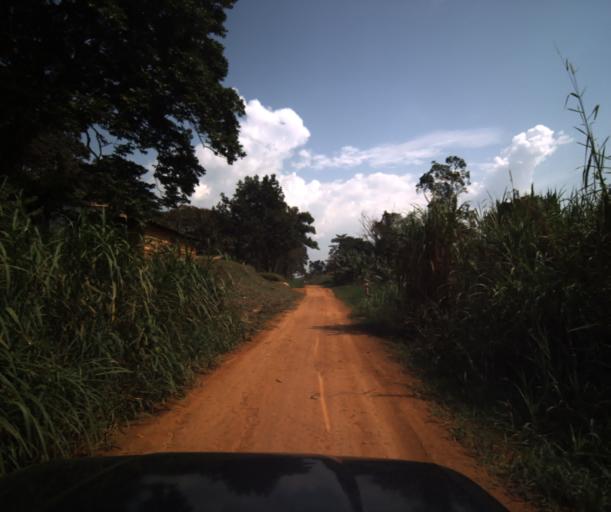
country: CM
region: Centre
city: Akono
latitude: 3.5953
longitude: 11.2406
